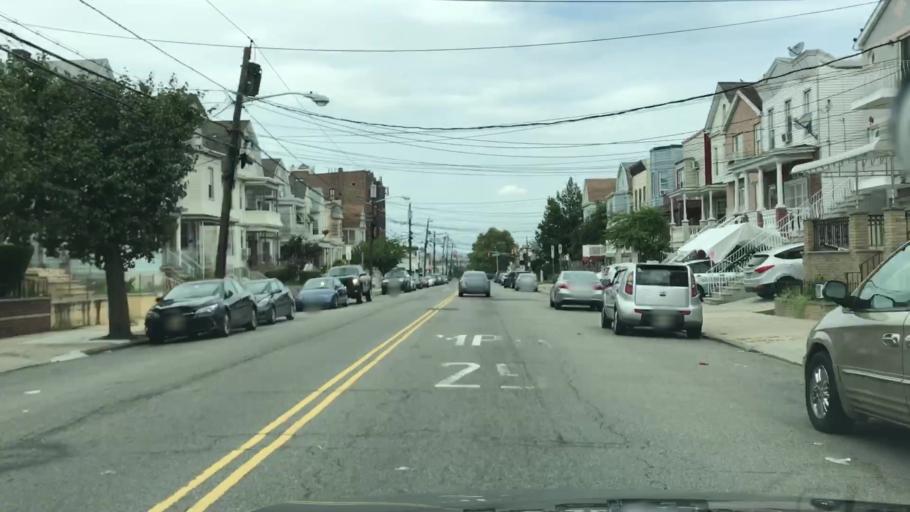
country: US
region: New Jersey
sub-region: Hudson County
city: Jersey City
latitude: 40.6987
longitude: -74.0932
